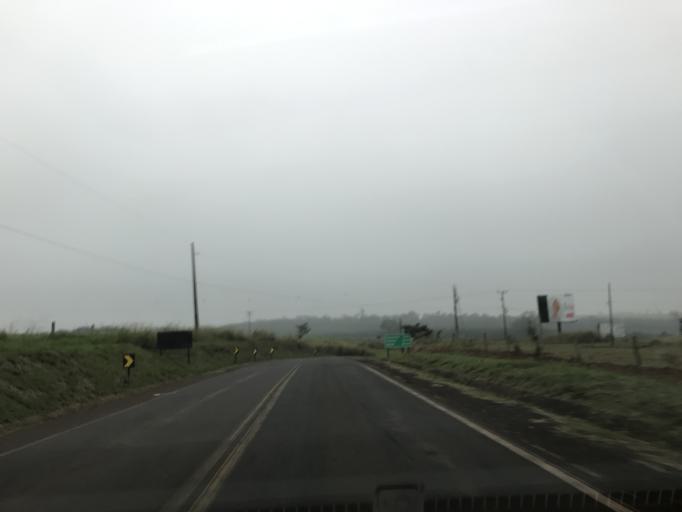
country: PY
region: Canindeyu
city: Salto del Guaira
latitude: -24.0832
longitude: -54.0936
